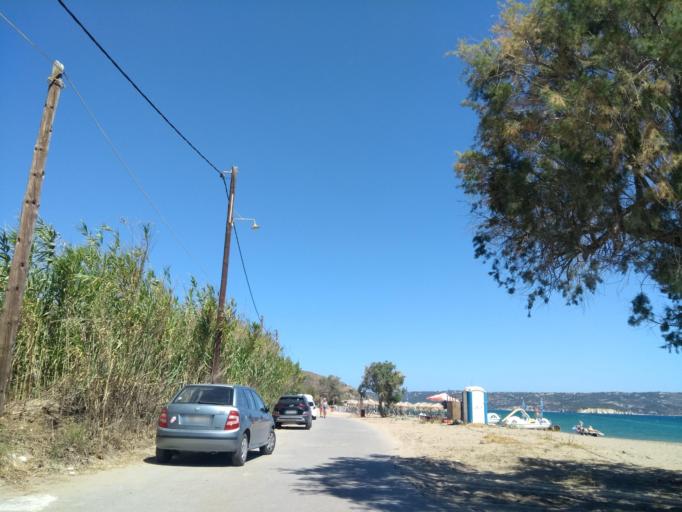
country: GR
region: Crete
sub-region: Nomos Chanias
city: Kalivai
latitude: 35.4613
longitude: 24.1608
